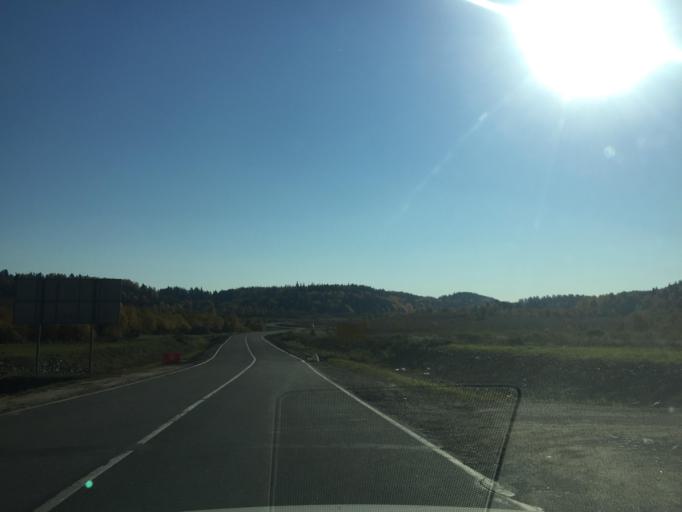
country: RU
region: Leningrad
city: Kuznechnoye
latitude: 61.3388
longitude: 29.8598
